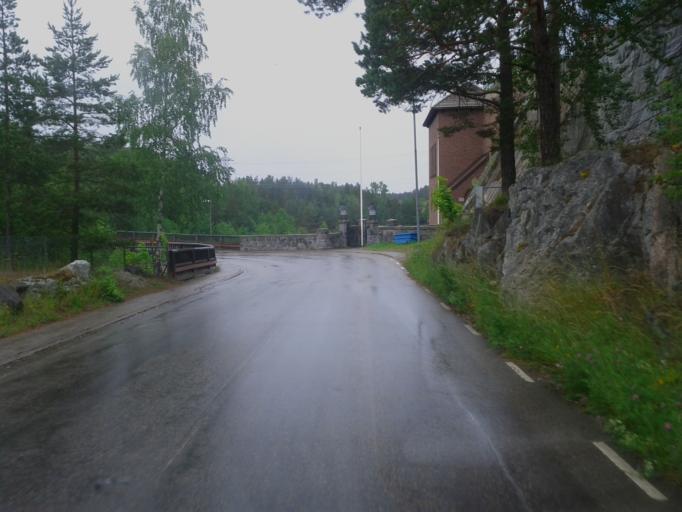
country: SE
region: Uppsala
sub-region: Alvkarleby Kommun
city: AElvkarleby
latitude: 60.5631
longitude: 17.4413
